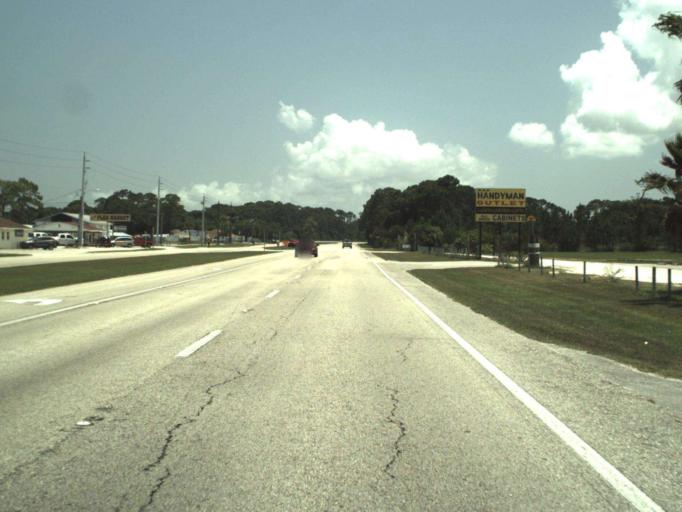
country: US
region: Florida
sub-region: Volusia County
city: Oak Hill
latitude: 28.8787
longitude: -80.8539
